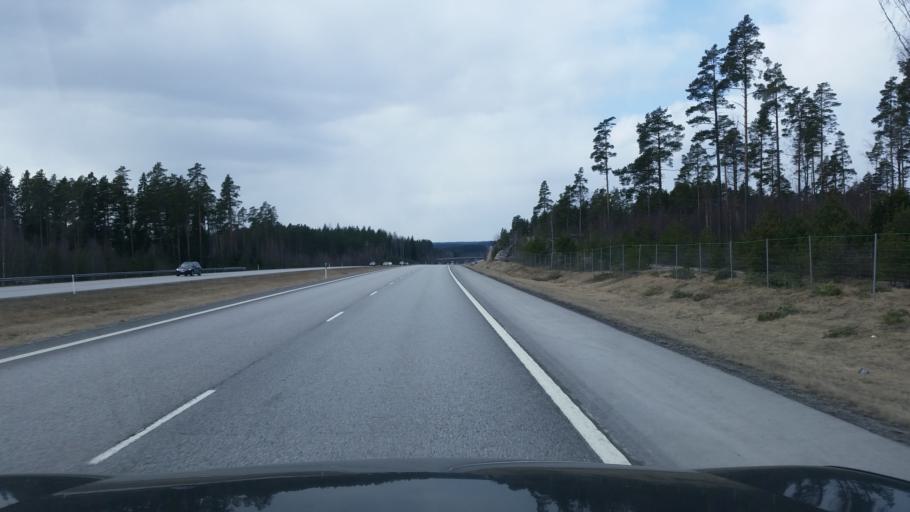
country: FI
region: Varsinais-Suomi
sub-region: Loimaa
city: Marttila
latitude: 60.4287
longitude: 22.8870
